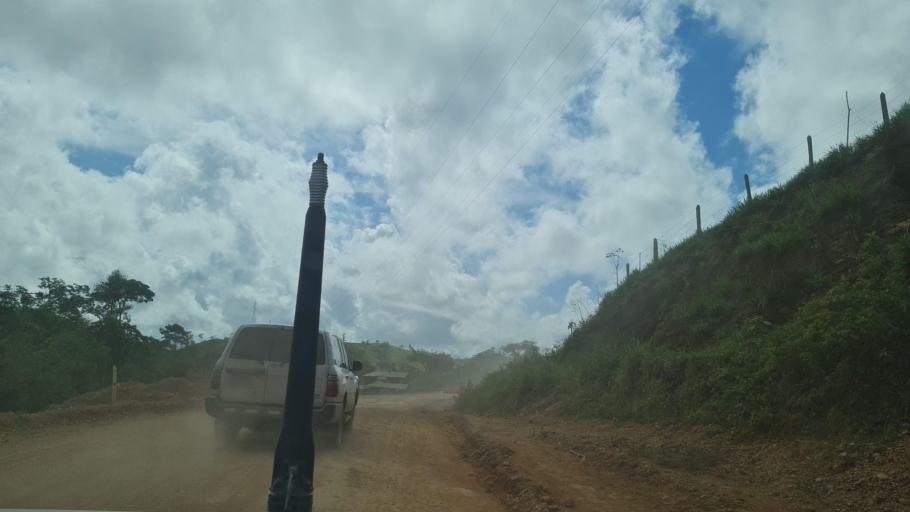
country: NI
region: Atlantico Norte (RAAN)
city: Puerto Cabezas
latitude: 14.1056
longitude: -83.7491
